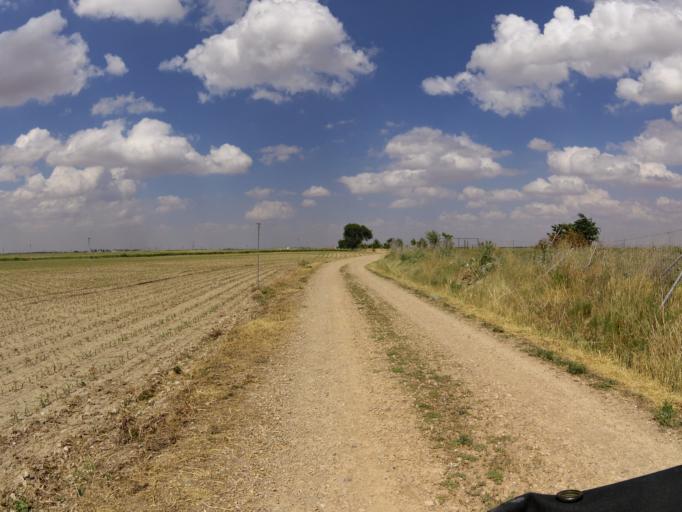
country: ES
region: Castille-La Mancha
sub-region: Provincia de Albacete
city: Pozuelo
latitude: 38.9192
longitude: -2.0080
